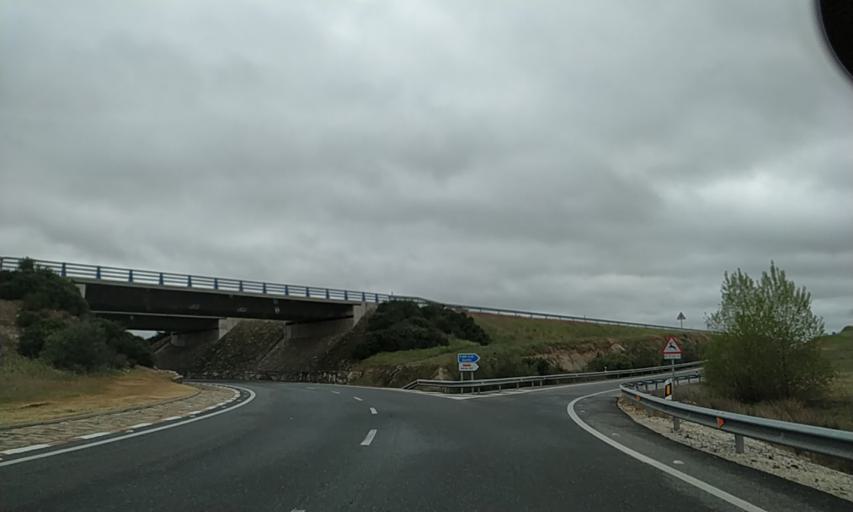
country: ES
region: Extremadura
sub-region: Provincia de Caceres
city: Caceres
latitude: 39.4614
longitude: -6.4224
